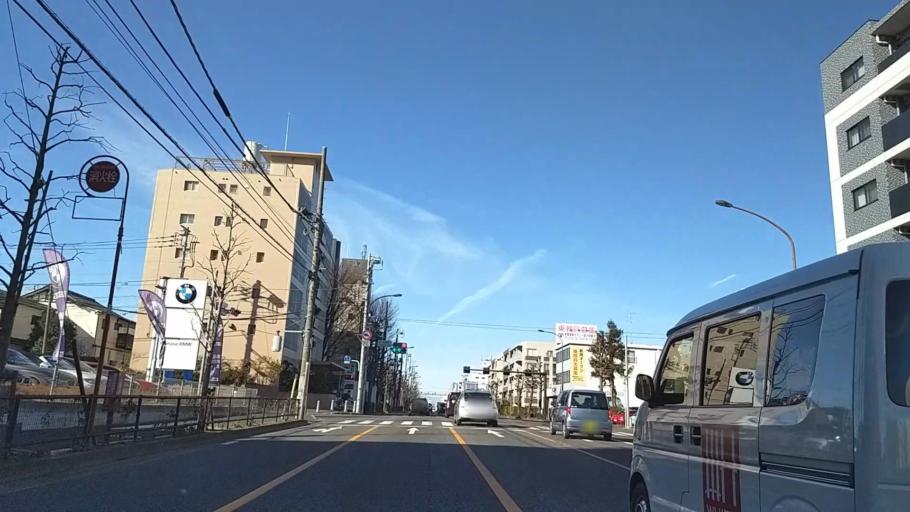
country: JP
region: Tokyo
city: Tokyo
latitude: 35.6006
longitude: 139.6648
